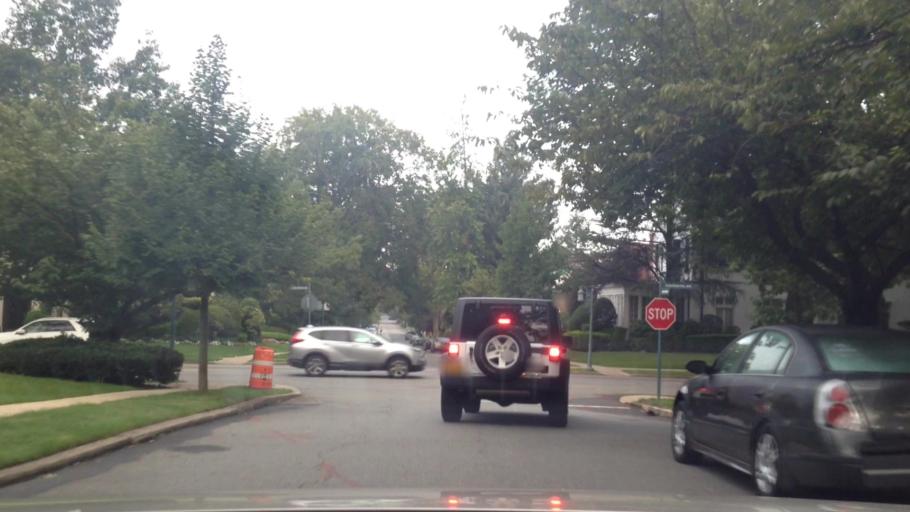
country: US
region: New York
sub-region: Queens County
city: Borough of Queens
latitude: 40.7170
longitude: -73.8463
